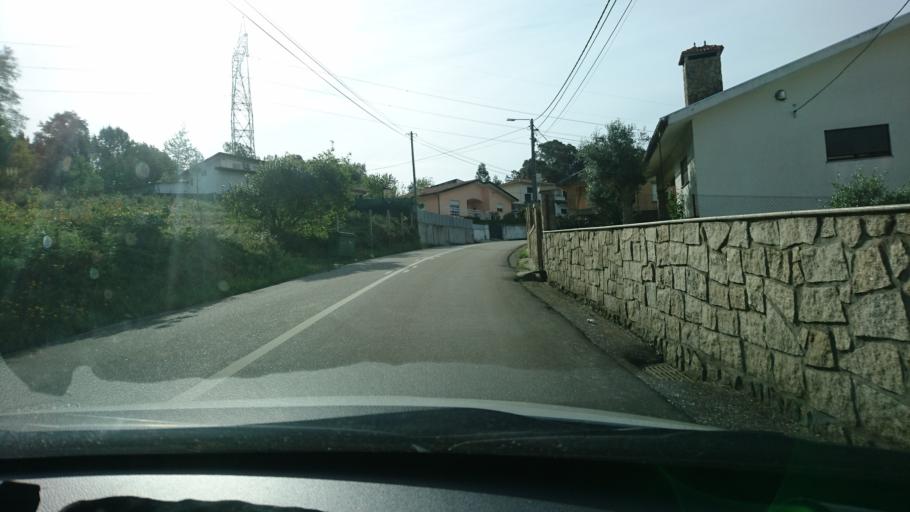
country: PT
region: Aveiro
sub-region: Oliveira de Azemeis
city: Sao Roque
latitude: 40.8786
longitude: -8.4791
